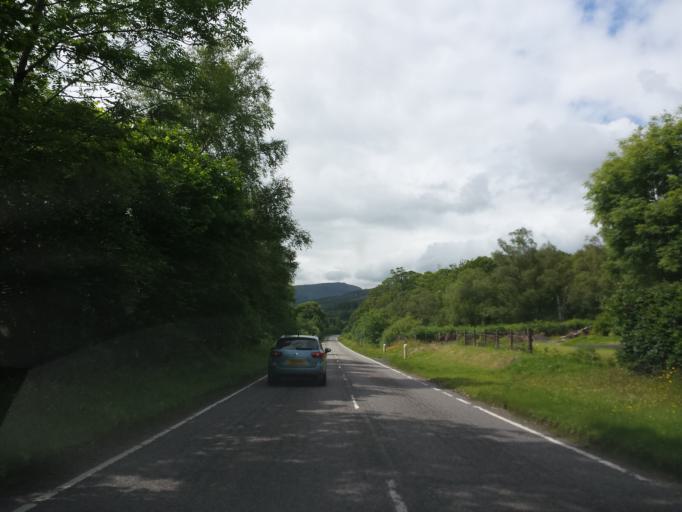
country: GB
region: Scotland
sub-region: Highland
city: Fort William
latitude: 56.8493
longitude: -5.1650
